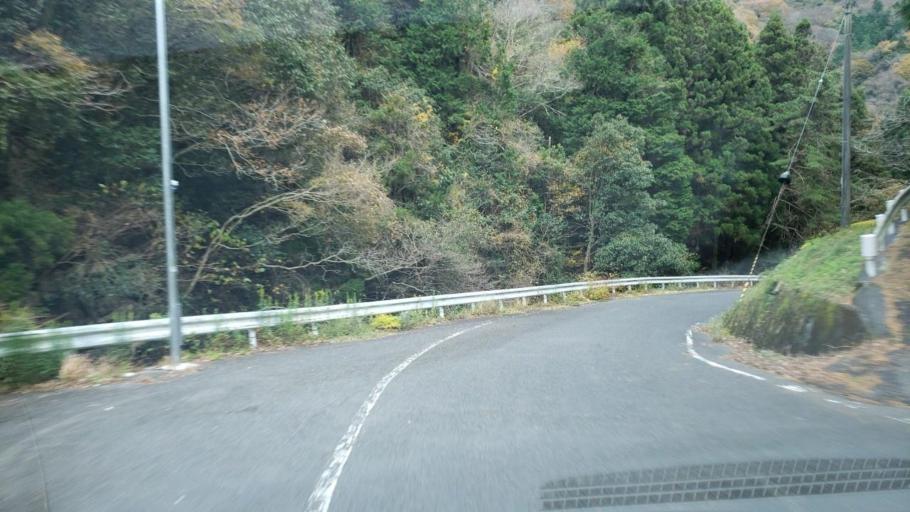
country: JP
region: Tokushima
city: Wakimachi
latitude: 34.1427
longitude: 134.2297
